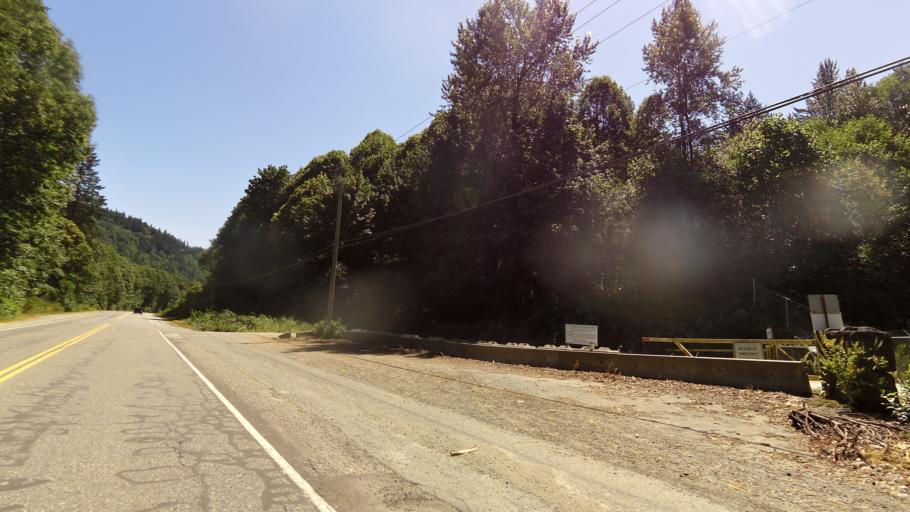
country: CA
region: British Columbia
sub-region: Fraser Valley Regional District
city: Chilliwack
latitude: 49.2247
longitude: -122.0145
